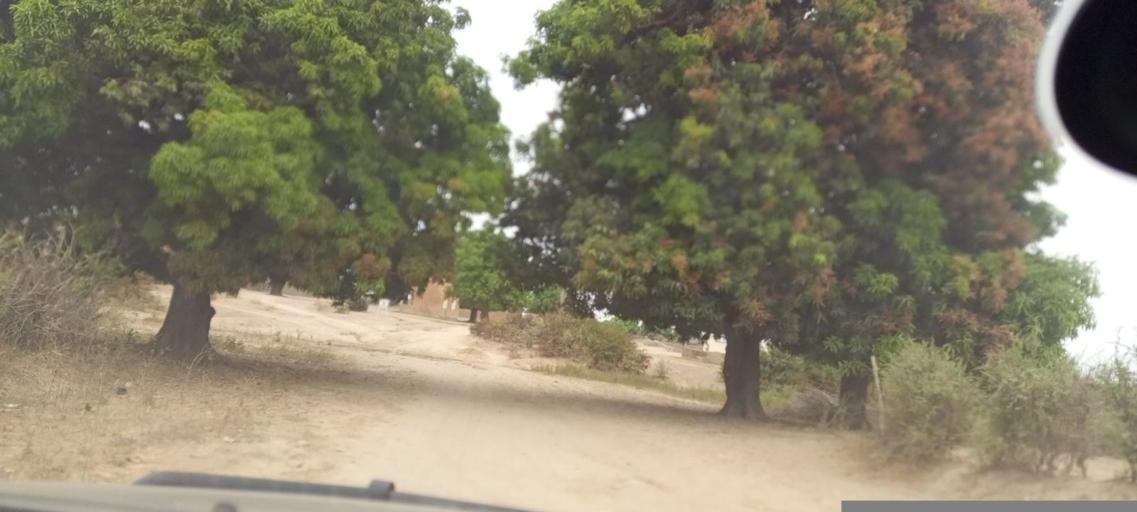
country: ML
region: Koulikoro
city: Kati
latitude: 12.7443
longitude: -8.3311
